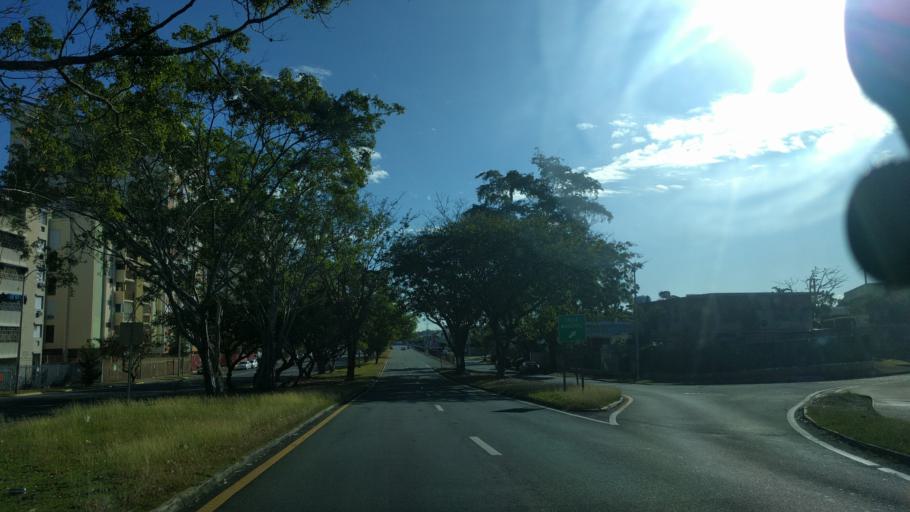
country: PR
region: Catano
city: Catano
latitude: 18.4245
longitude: -66.0545
